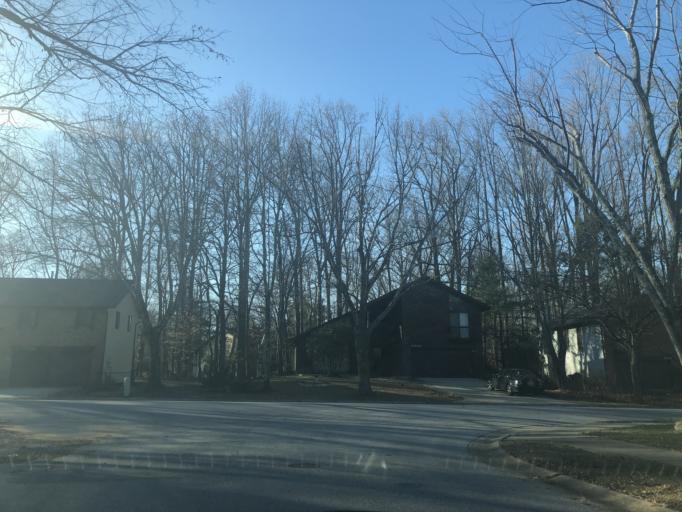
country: US
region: Maryland
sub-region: Howard County
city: Columbia
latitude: 39.2068
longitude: -76.8377
